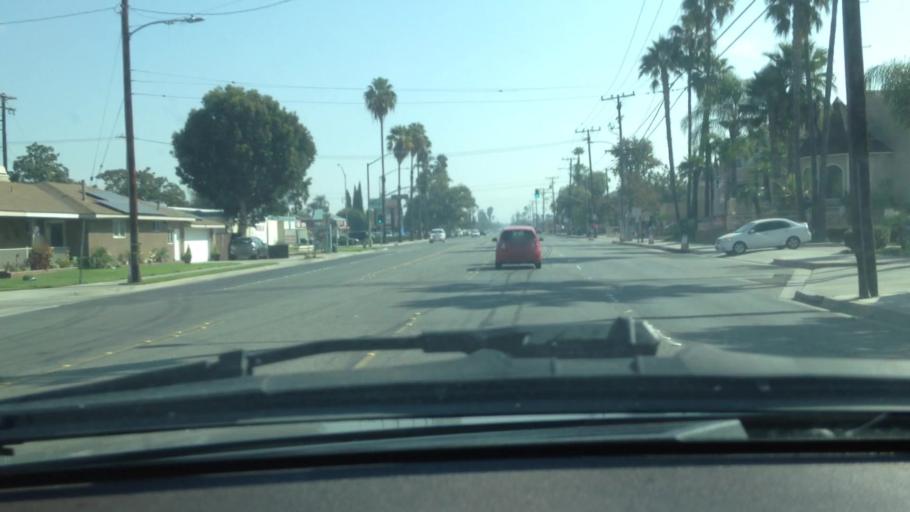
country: US
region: California
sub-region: Orange County
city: Anaheim
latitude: 33.8473
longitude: -117.8992
